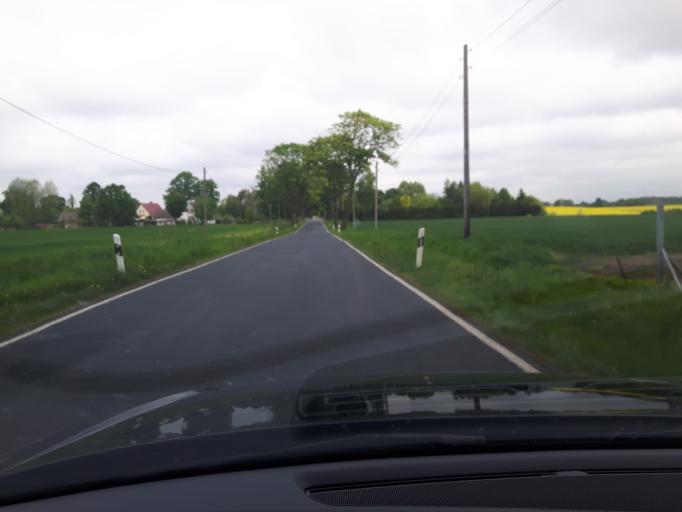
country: DE
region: Mecklenburg-Vorpommern
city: Bad Sulze
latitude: 54.1516
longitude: 12.7073
